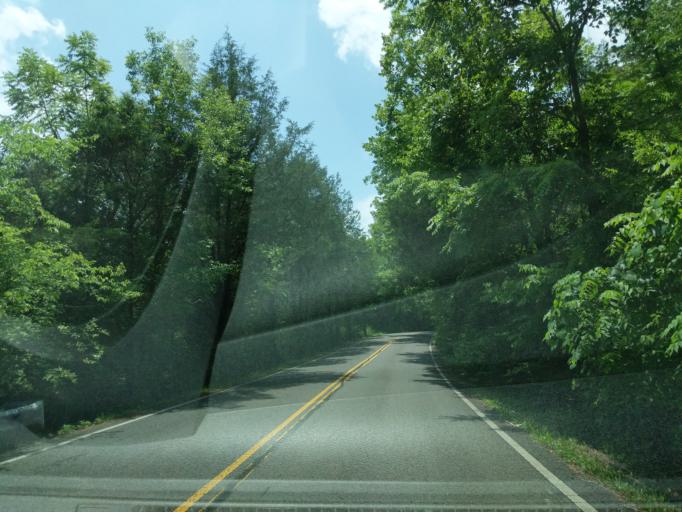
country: US
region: Tennessee
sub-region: Davidson County
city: Goodlettsville
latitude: 36.2996
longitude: -86.7313
